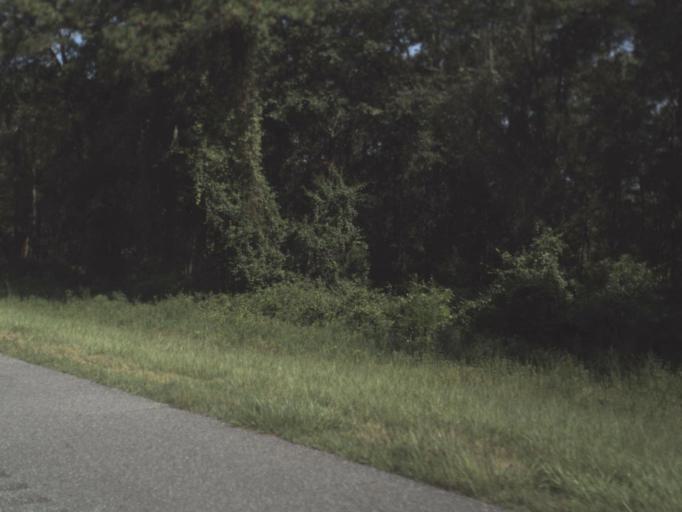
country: US
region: Florida
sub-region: Suwannee County
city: Wellborn
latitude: 30.2858
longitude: -82.8357
